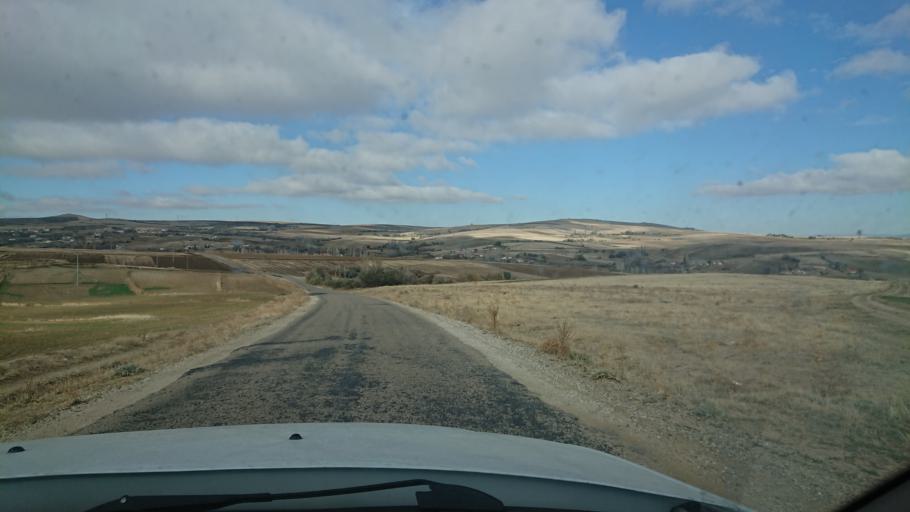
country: TR
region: Aksaray
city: Agacoren
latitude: 38.8178
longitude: 33.9801
